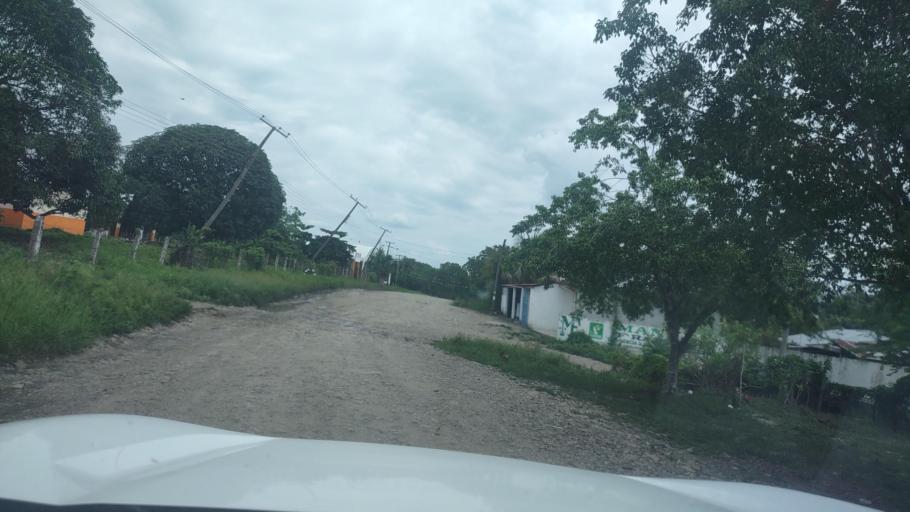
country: MX
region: Veracruz
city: Tepetzintla
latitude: 21.0490
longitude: -97.9994
